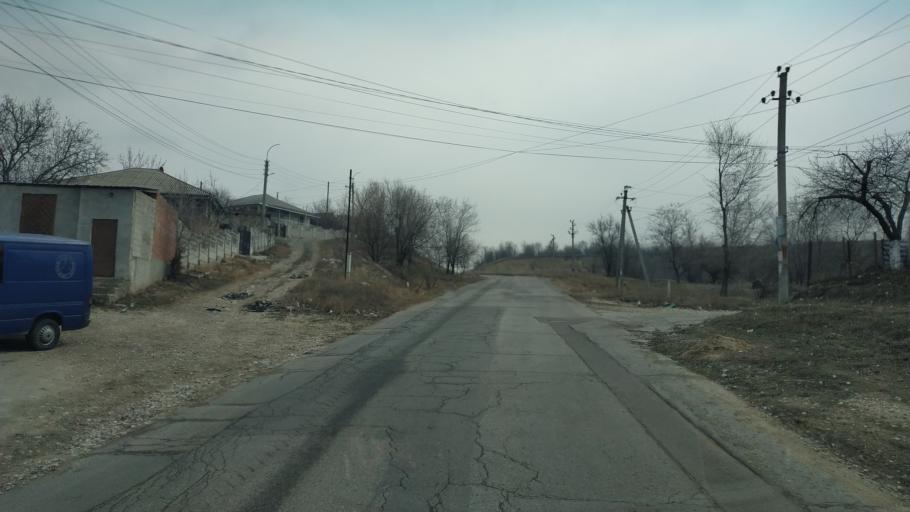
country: MD
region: Chisinau
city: Singera
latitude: 46.9172
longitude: 28.9852
